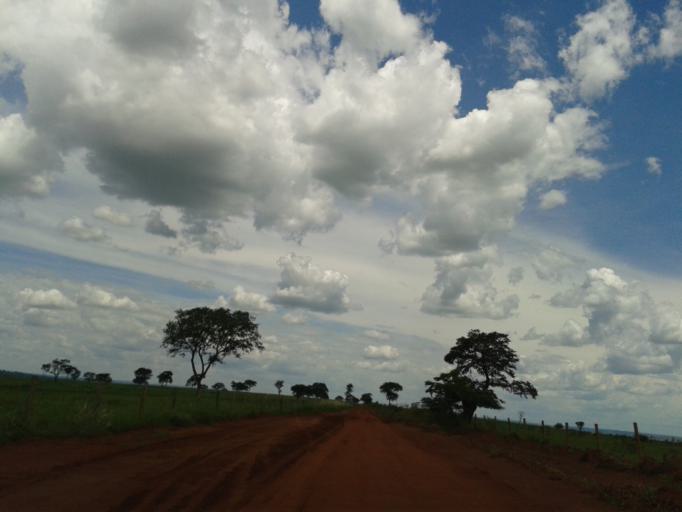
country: BR
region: Minas Gerais
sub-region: Ituiutaba
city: Ituiutaba
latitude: -18.8889
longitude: -49.4680
